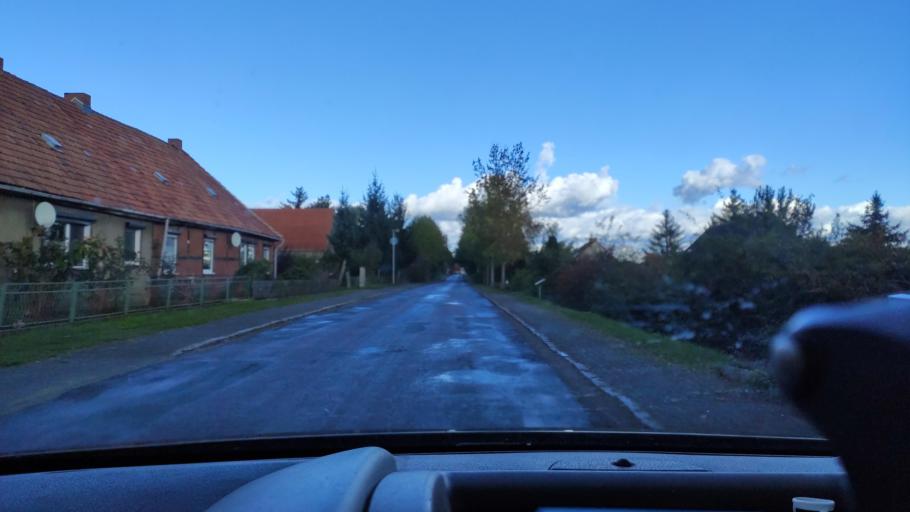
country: DE
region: Mecklenburg-Vorpommern
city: Tarnow
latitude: 53.7931
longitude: 11.9919
